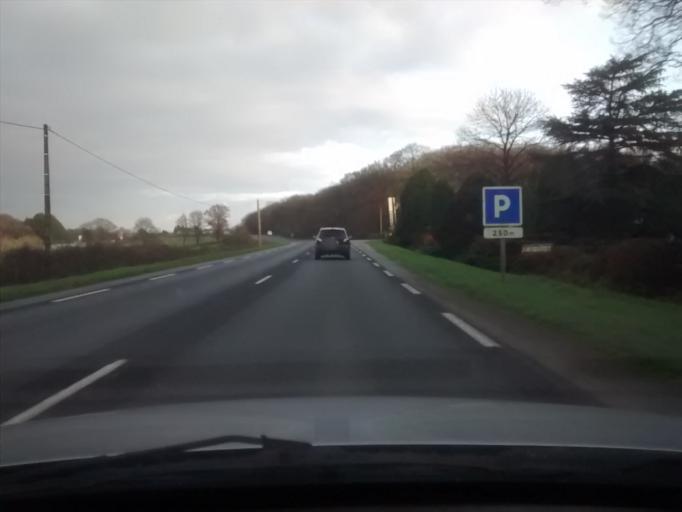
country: FR
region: Pays de la Loire
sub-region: Departement de la Mayenne
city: Port-Brillet
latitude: 48.0758
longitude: -0.9870
